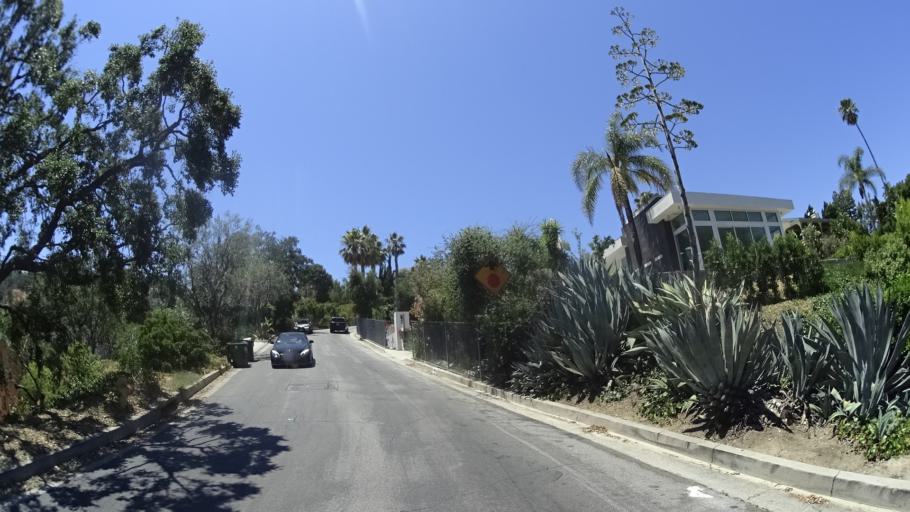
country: US
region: California
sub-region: Los Angeles County
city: Universal City
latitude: 34.1353
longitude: -118.3736
